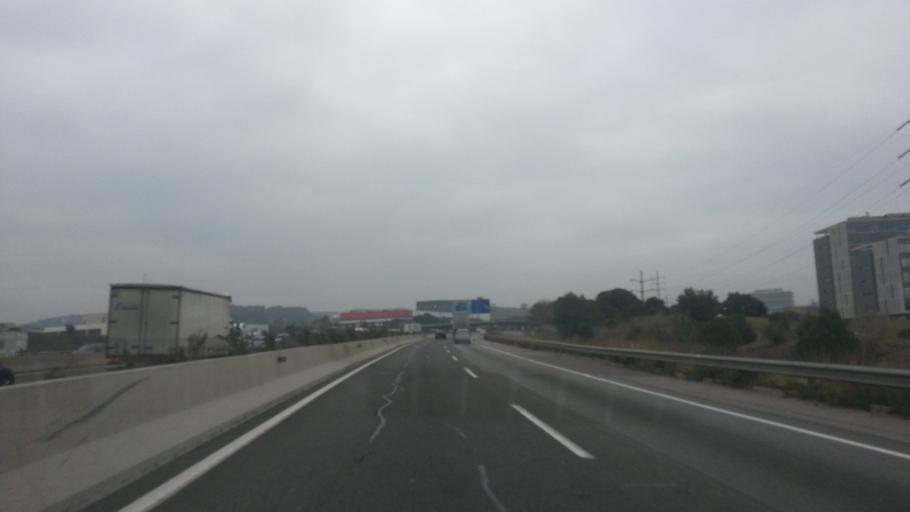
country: ES
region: Catalonia
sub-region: Provincia de Barcelona
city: Rubi
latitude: 41.4846
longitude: 2.0500
